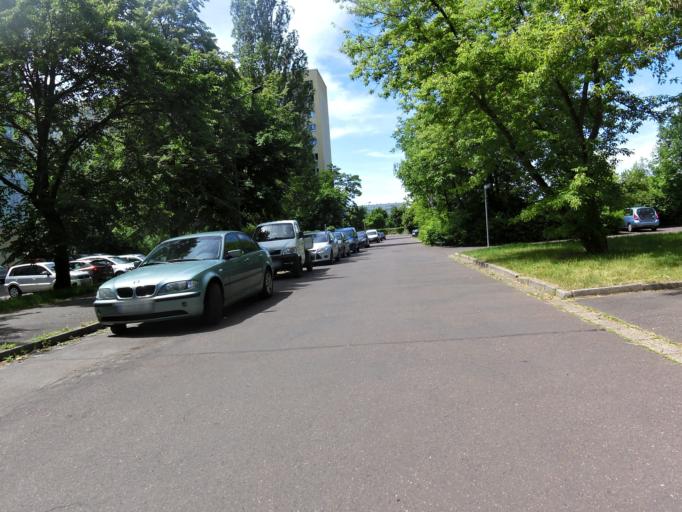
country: DE
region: Saxony
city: Markkleeberg
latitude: 51.3026
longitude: 12.4031
